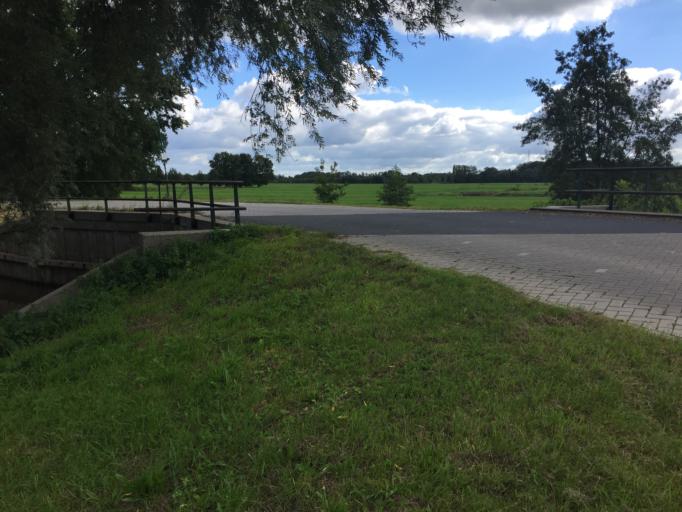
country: NL
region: Utrecht
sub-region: Stichtse Vecht
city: Spechtenkamp
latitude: 52.1615
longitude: 5.0268
